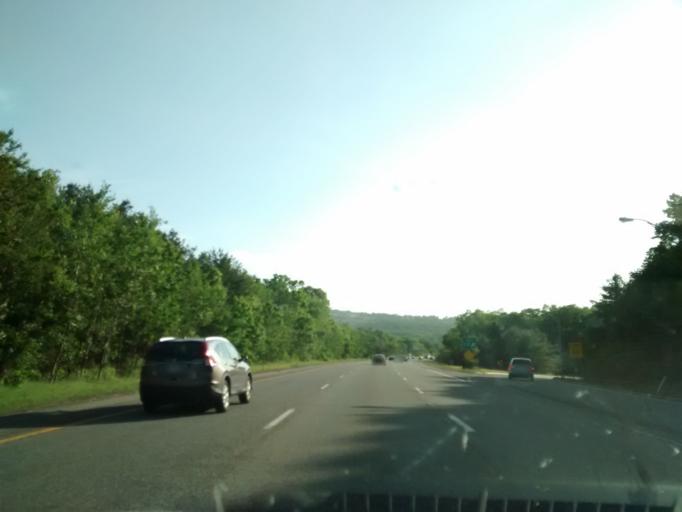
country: US
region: Massachusetts
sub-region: Worcester County
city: Shrewsbury
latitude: 42.2969
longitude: -71.7462
